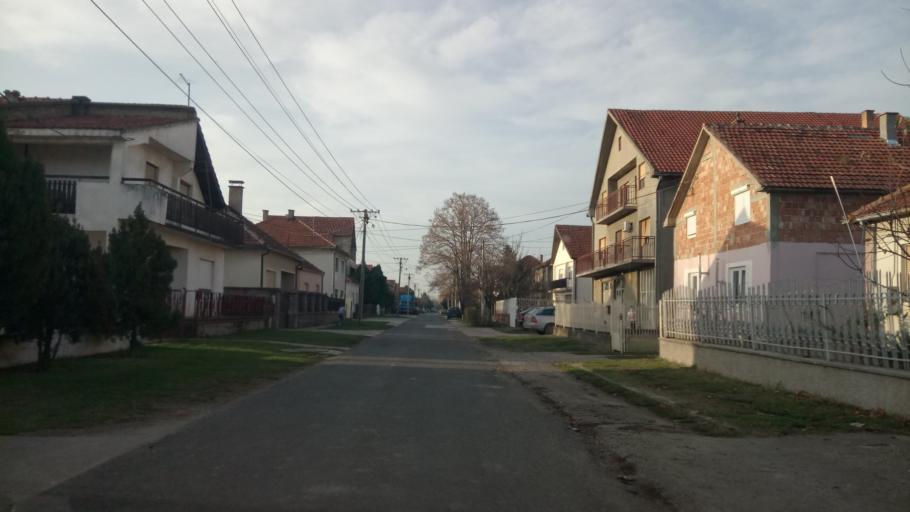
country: RS
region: Autonomna Pokrajina Vojvodina
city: Nova Pazova
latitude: 44.9357
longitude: 20.2255
